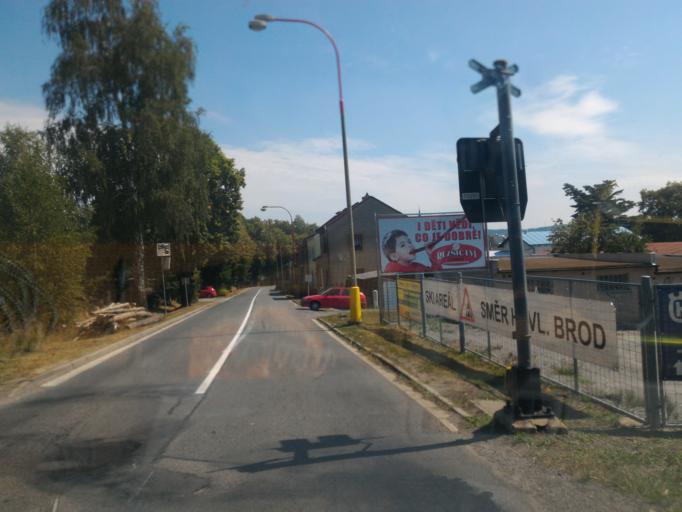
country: CZ
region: Pardubicky
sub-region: Okres Chrudim
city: Hlinsko
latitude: 49.7628
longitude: 15.8955
